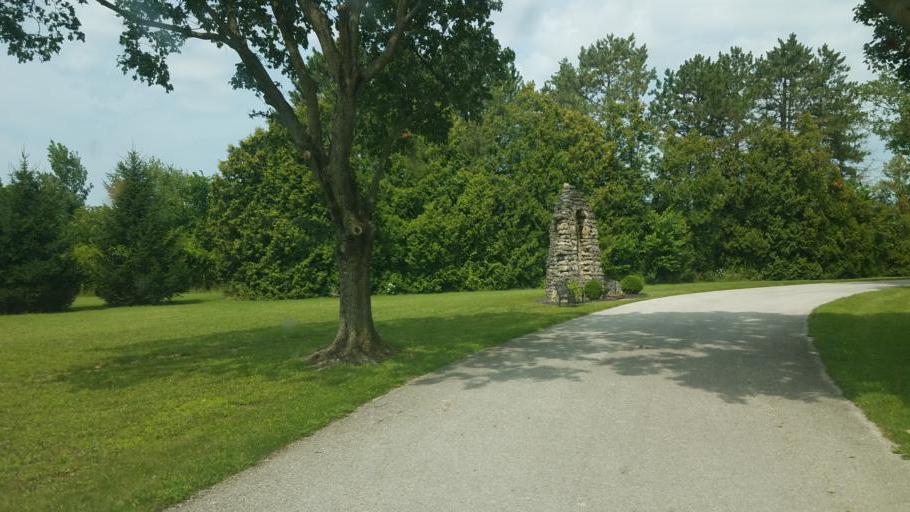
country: US
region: Ohio
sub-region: Wyandot County
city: Carey
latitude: 40.9493
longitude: -83.3957
